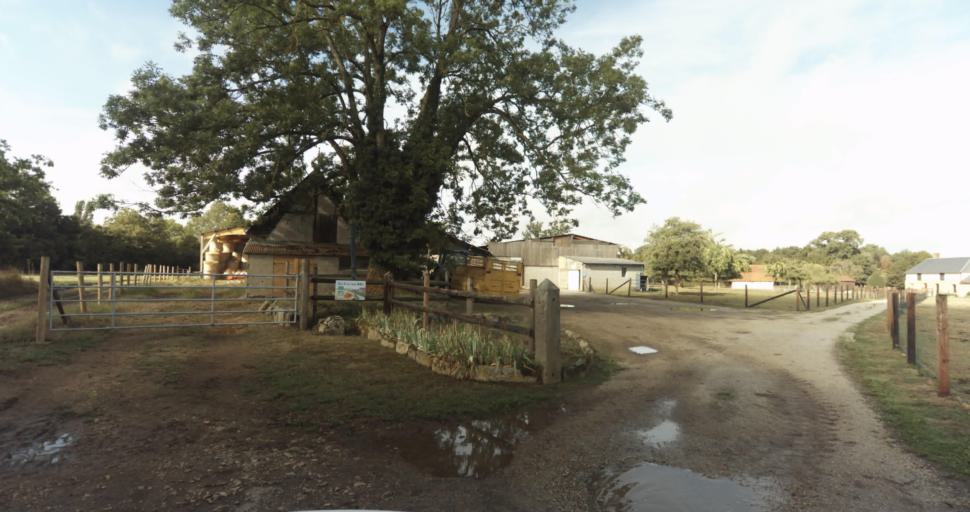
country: FR
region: Lower Normandy
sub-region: Departement de l'Orne
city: Gace
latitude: 48.8709
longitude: 0.3234
